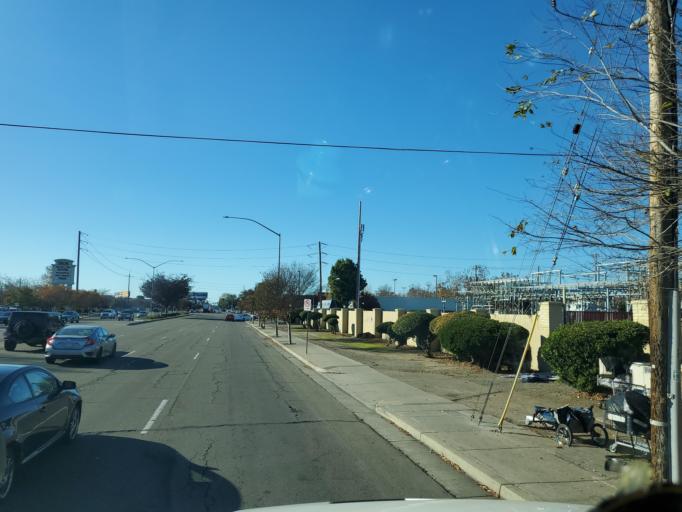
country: US
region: California
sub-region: San Joaquin County
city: Lincoln Village
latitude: 38.0210
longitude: -121.3198
